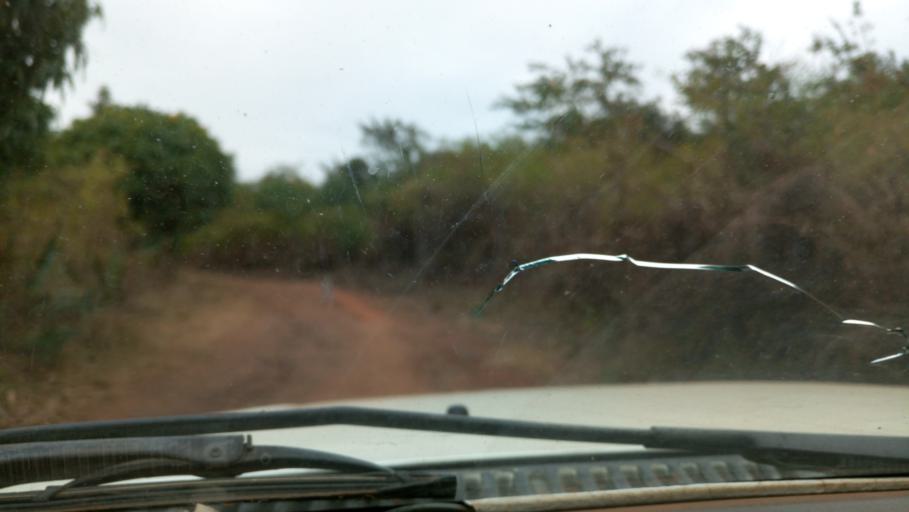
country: KE
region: Murang'a District
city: Maragua
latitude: -0.8348
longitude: 37.2168
